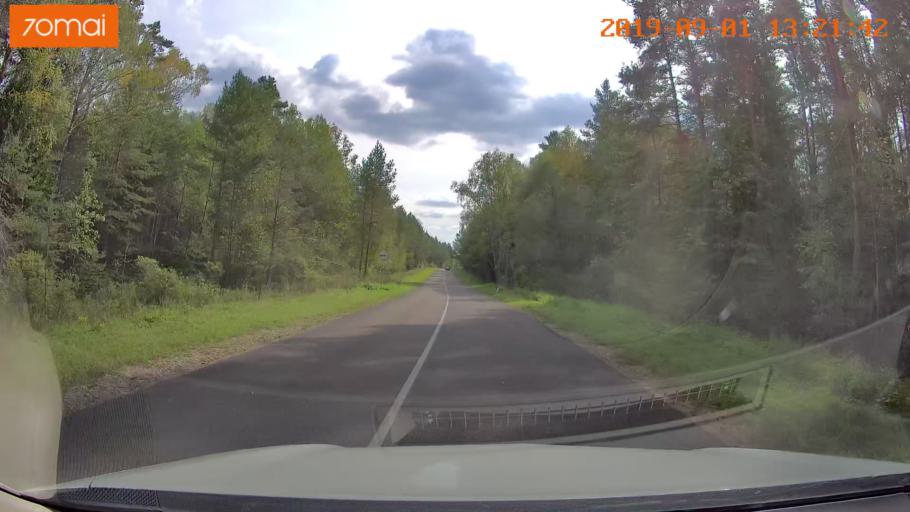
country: RU
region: Kaluga
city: Maloyaroslavets
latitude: 54.9001
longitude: 36.5168
